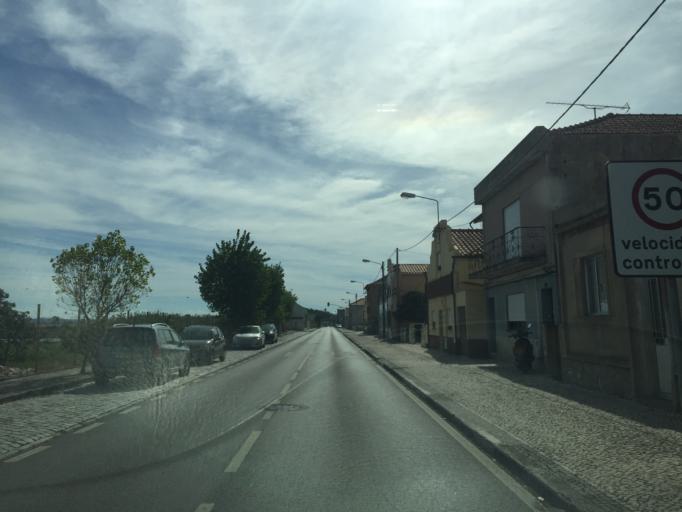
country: PT
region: Coimbra
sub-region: Figueira da Foz
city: Figueira da Foz
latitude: 40.1278
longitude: -8.8532
